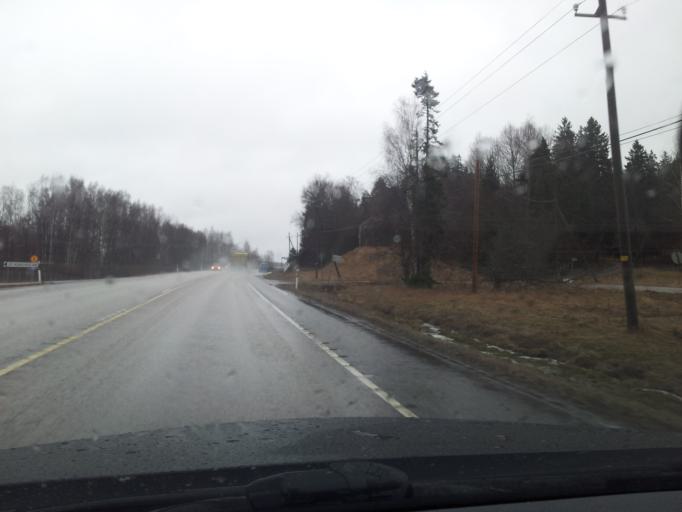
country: FI
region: Uusimaa
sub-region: Helsinki
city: Kirkkonummi
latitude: 60.1576
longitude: 24.5416
